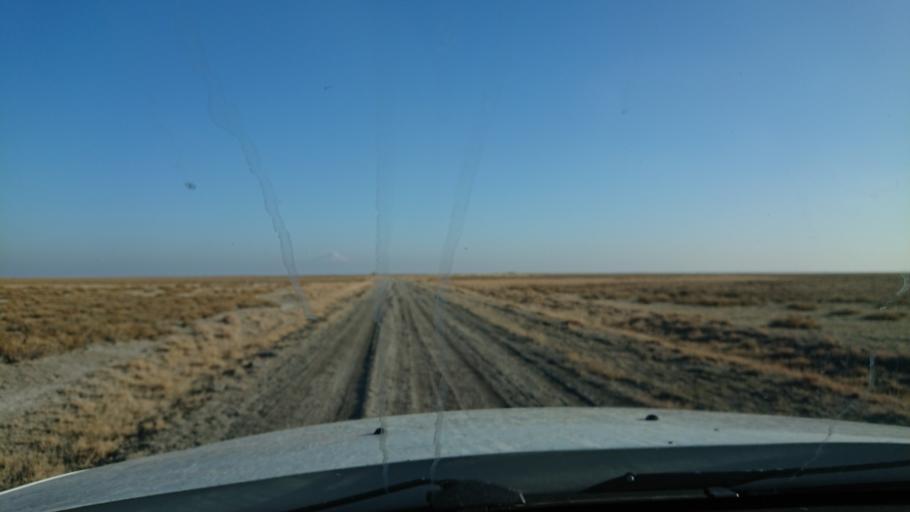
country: TR
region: Aksaray
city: Sultanhani
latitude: 38.4010
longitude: 33.5806
